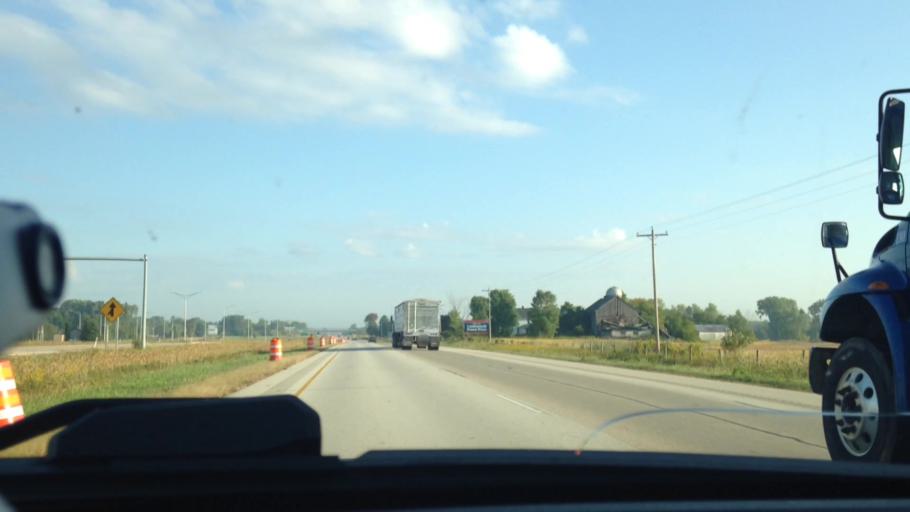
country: US
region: Wisconsin
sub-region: Brown County
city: Suamico
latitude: 44.7392
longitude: -88.0506
